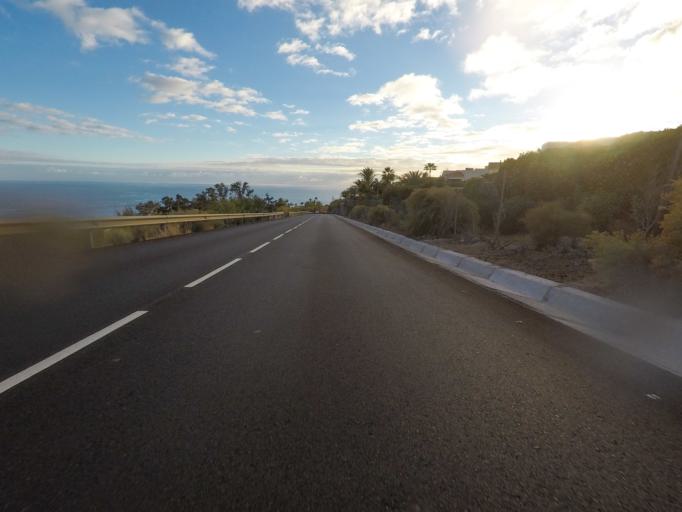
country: ES
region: Canary Islands
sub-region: Provincia de Santa Cruz de Tenerife
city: Alajero
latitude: 28.0437
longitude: -17.1937
